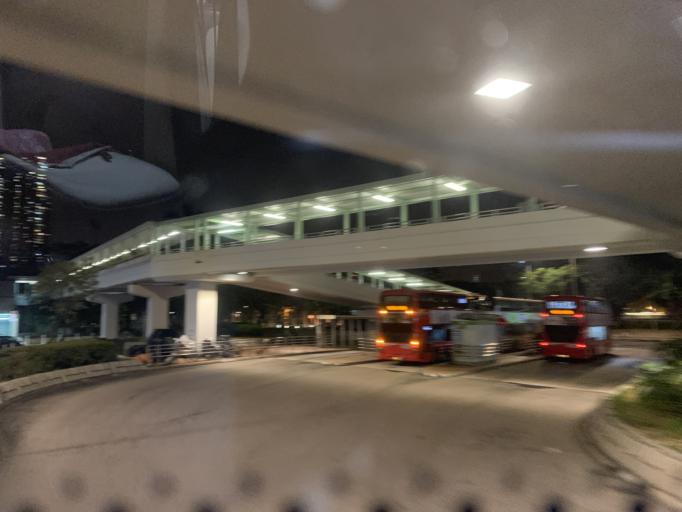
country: HK
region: Tsuen Wan
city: Tsuen Wan
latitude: 22.3534
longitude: 114.1085
